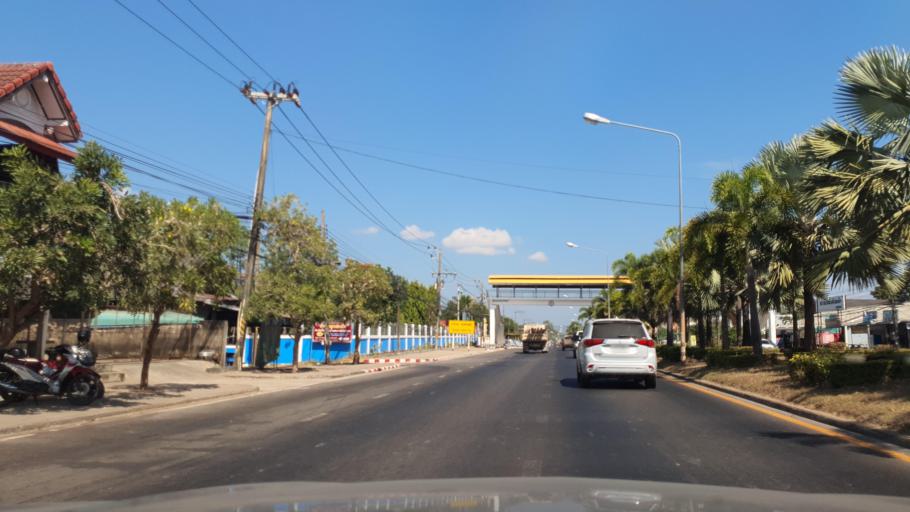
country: TH
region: Kalasin
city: Somdet
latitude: 16.7061
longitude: 103.7494
